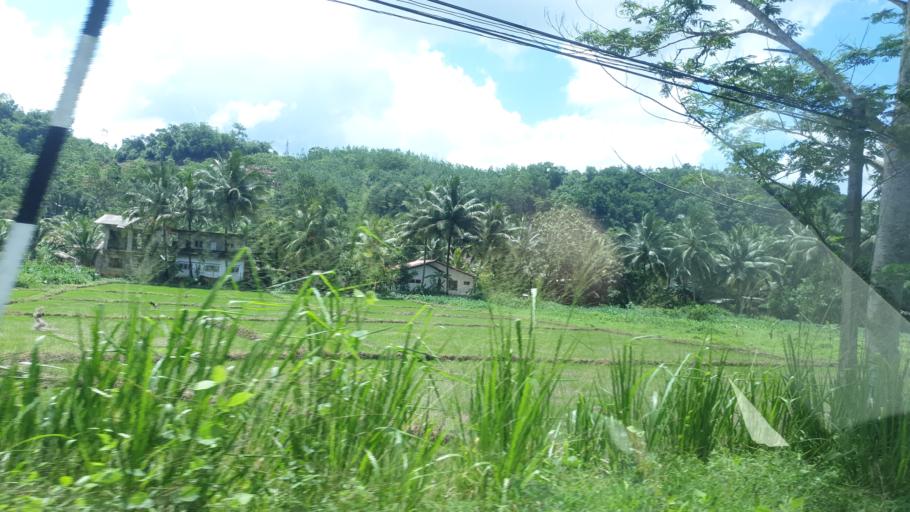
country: LK
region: Western
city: Horawala Junction
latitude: 6.5221
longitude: 80.2189
